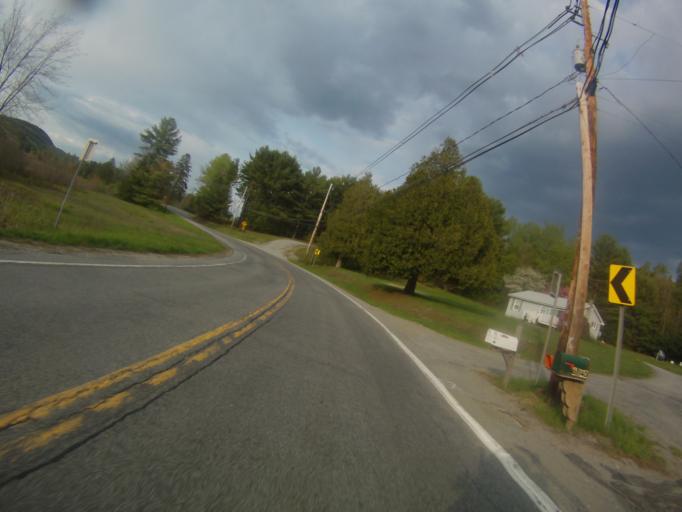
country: US
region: New York
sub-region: Warren County
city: Warrensburg
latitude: 43.6860
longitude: -73.7357
